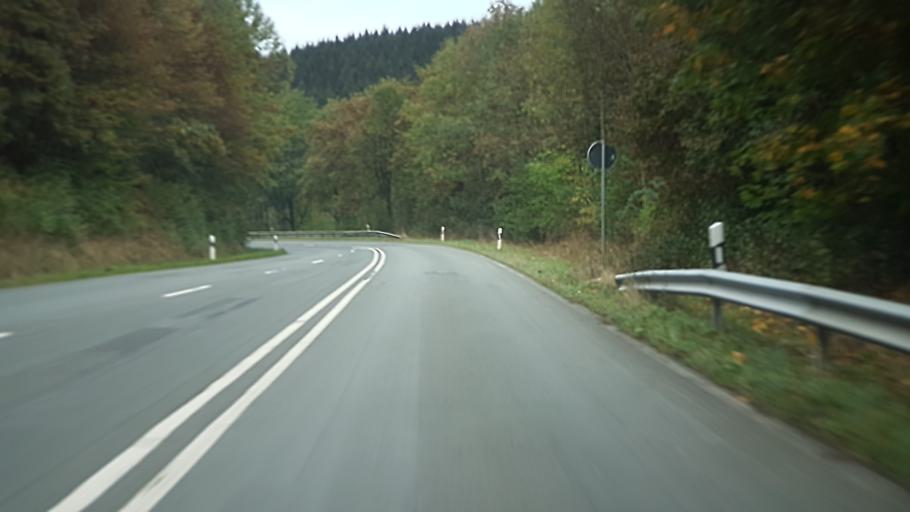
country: DE
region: North Rhine-Westphalia
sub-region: Regierungsbezirk Arnsberg
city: Attendorn
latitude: 51.1439
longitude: 7.8780
